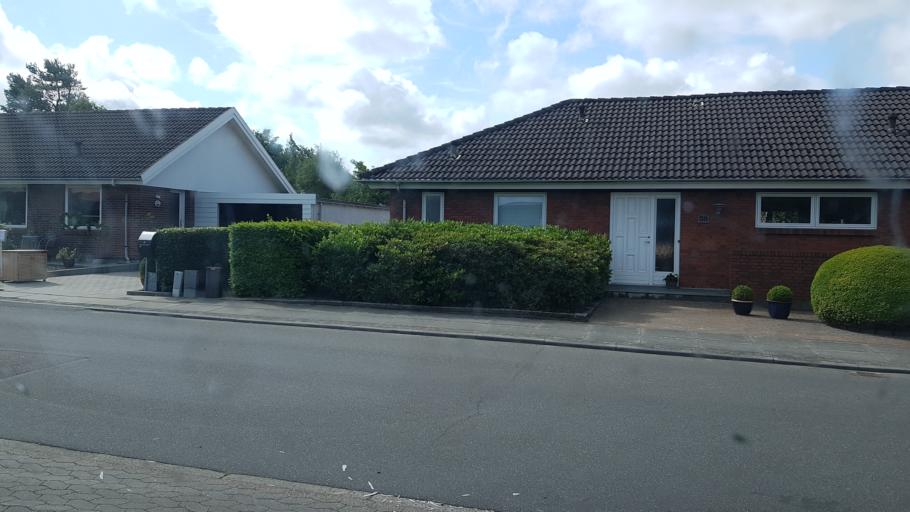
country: DK
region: South Denmark
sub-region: Varde Kommune
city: Oksbol
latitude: 55.6240
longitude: 8.2787
